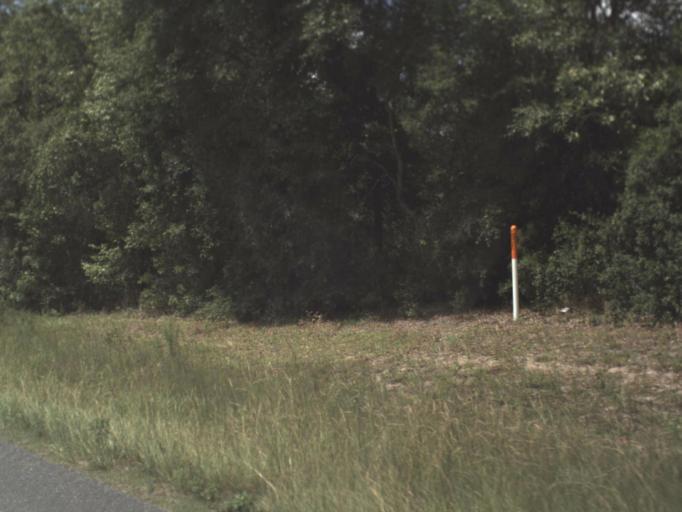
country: US
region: Florida
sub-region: Gilchrist County
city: Trenton
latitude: 29.8009
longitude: -82.8670
